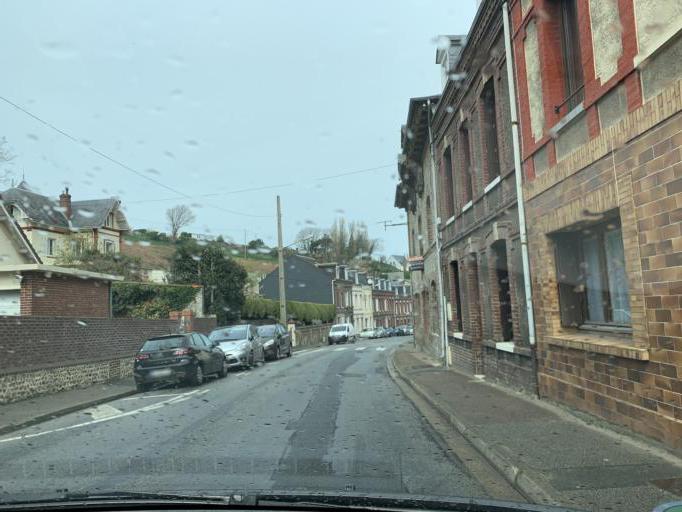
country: FR
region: Haute-Normandie
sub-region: Departement de la Seine-Maritime
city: Fecamp
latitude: 49.7555
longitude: 0.3628
